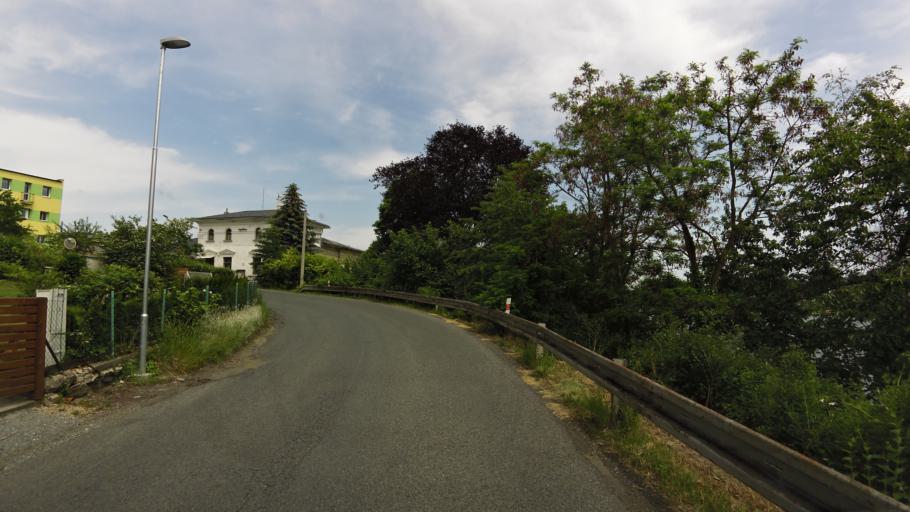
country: CZ
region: Plzensky
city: Holoubkov
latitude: 49.7753
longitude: 13.6951
